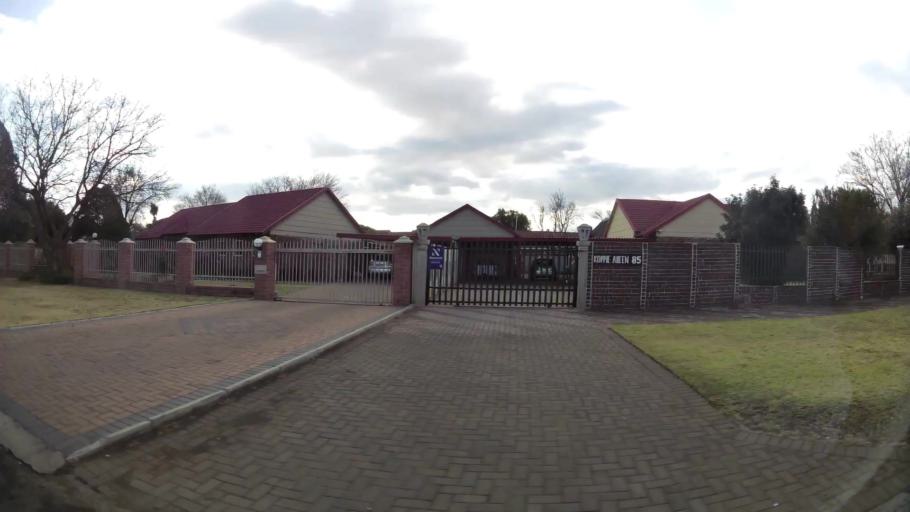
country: ZA
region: Orange Free State
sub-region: Lejweleputswa District Municipality
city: Welkom
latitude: -27.9998
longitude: 26.7396
